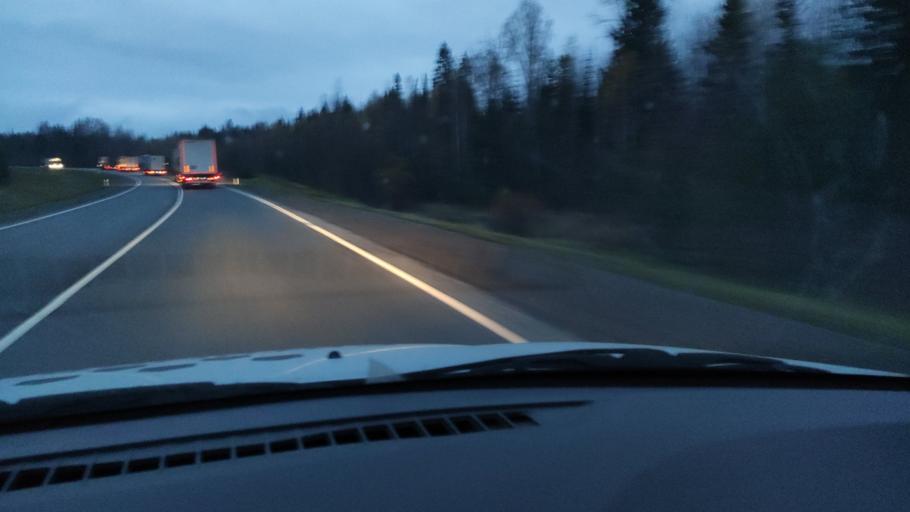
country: RU
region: Kirov
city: Kostino
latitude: 58.8271
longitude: 53.4236
